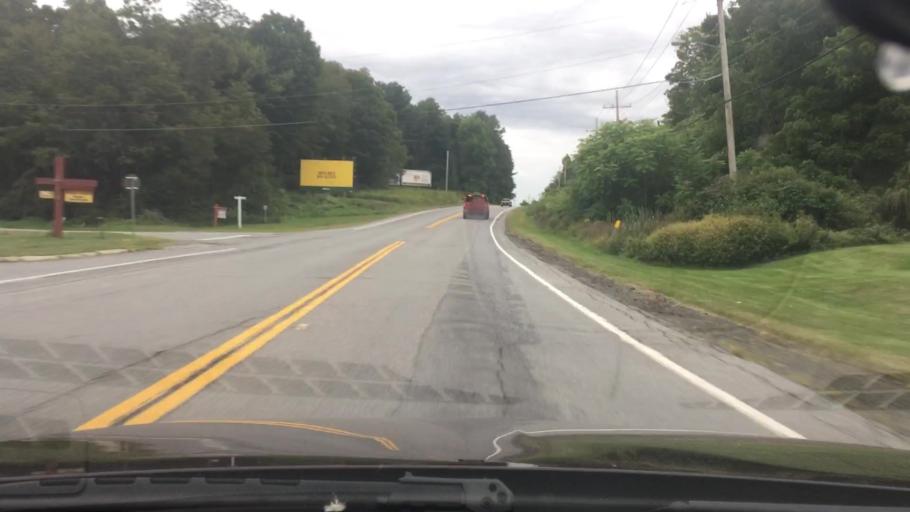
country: US
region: New York
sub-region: Dutchess County
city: Pleasant Valley
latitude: 41.7735
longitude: -73.7708
